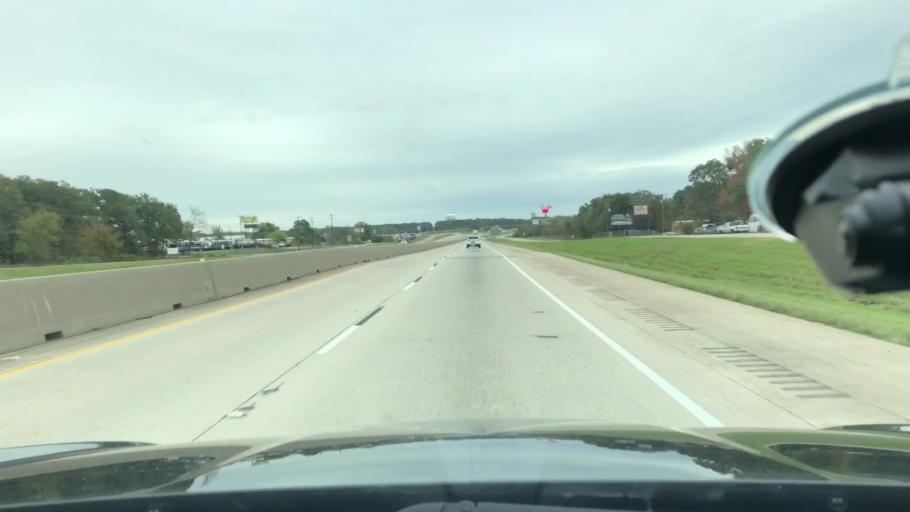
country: US
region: Texas
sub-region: Hopkins County
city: Sulphur Springs
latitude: 33.1206
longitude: -95.6481
